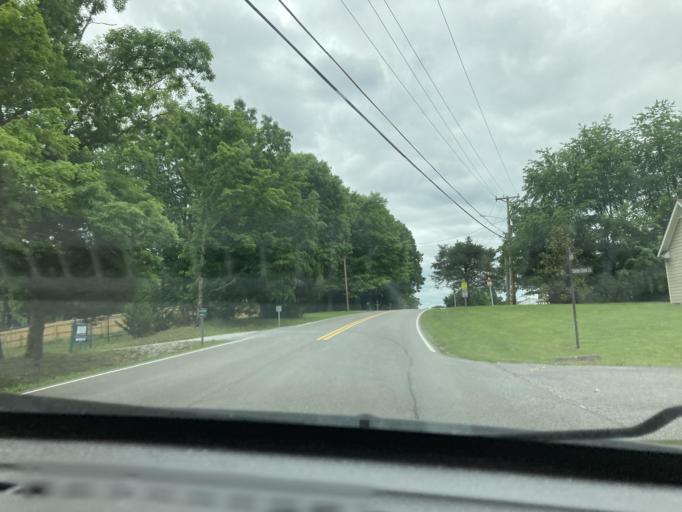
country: US
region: Tennessee
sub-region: Dickson County
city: Dickson
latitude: 36.0487
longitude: -87.3677
